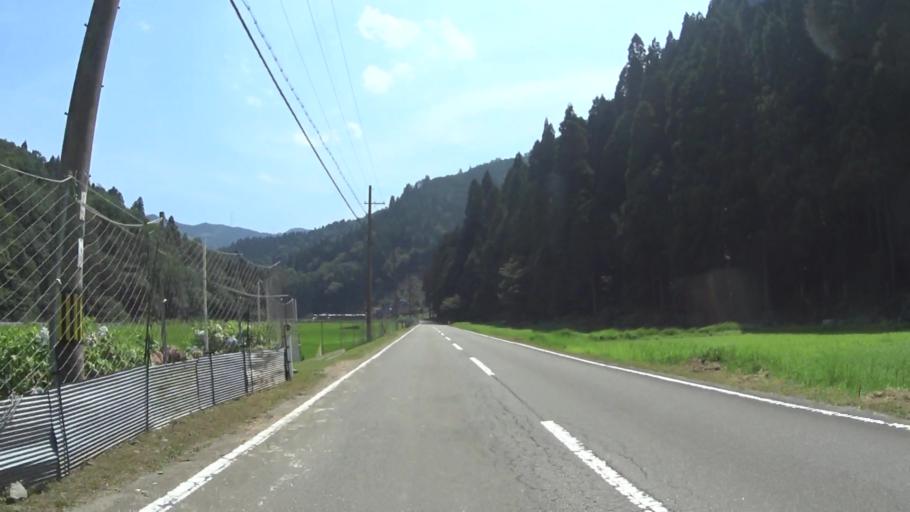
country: JP
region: Kyoto
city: Maizuru
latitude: 35.3393
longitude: 135.5338
